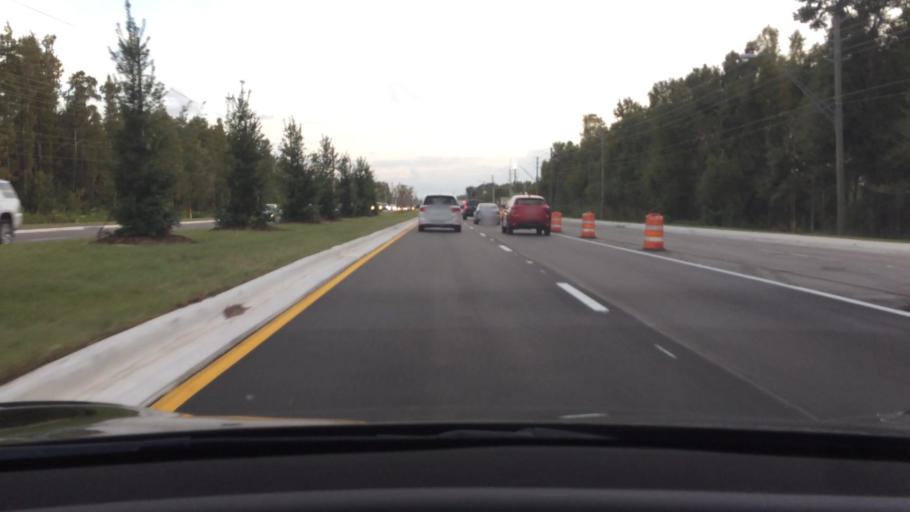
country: US
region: Florida
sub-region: Hillsborough County
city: Pebble Creek
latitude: 28.1663
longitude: -82.3537
